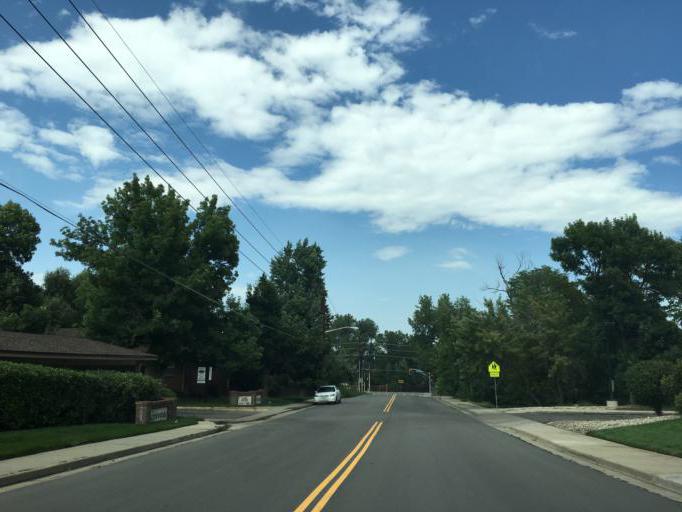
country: US
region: Colorado
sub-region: Jefferson County
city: Applewood
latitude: 39.7460
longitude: -105.1189
